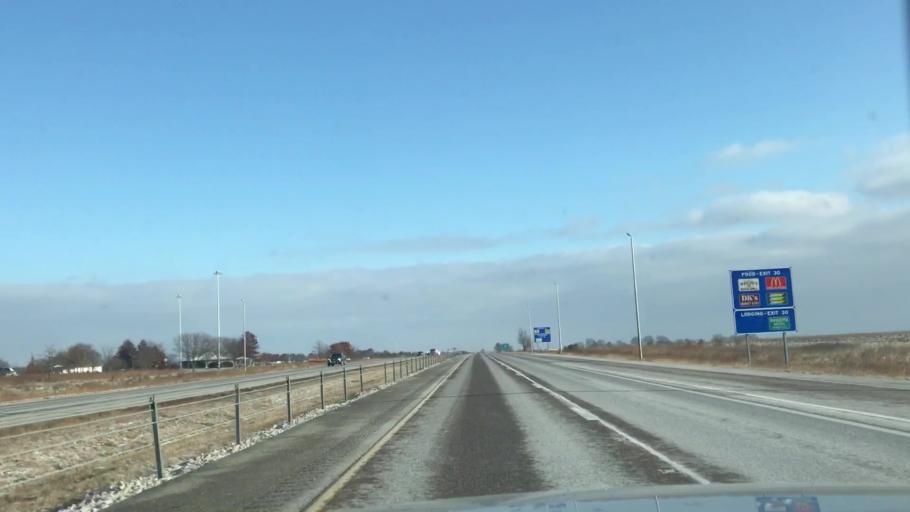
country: US
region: Illinois
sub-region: Madison County
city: Worden
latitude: 38.8694
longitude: -89.8518
